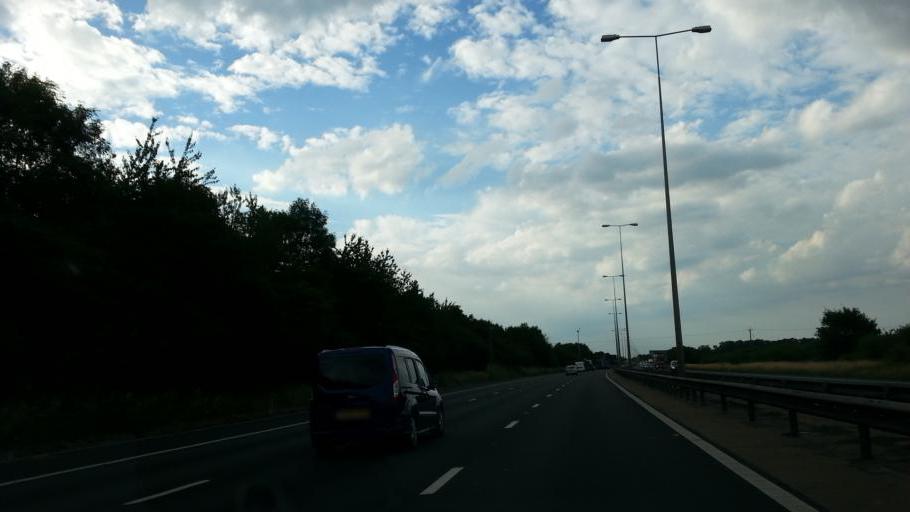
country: GB
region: England
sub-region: Worcestershire
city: Kempsey
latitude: 52.1143
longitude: -2.1967
